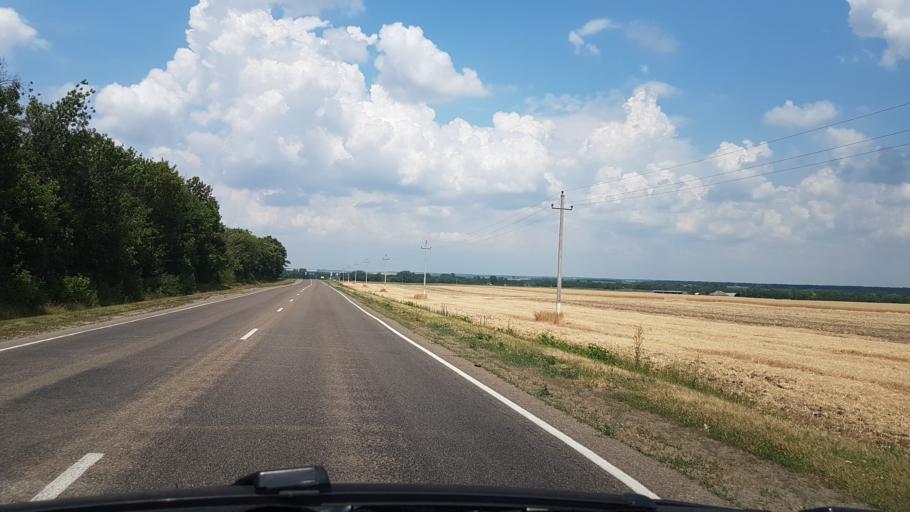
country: RU
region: Krasnodarskiy
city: Dmitriyevskaya
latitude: 45.6943
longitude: 40.7442
